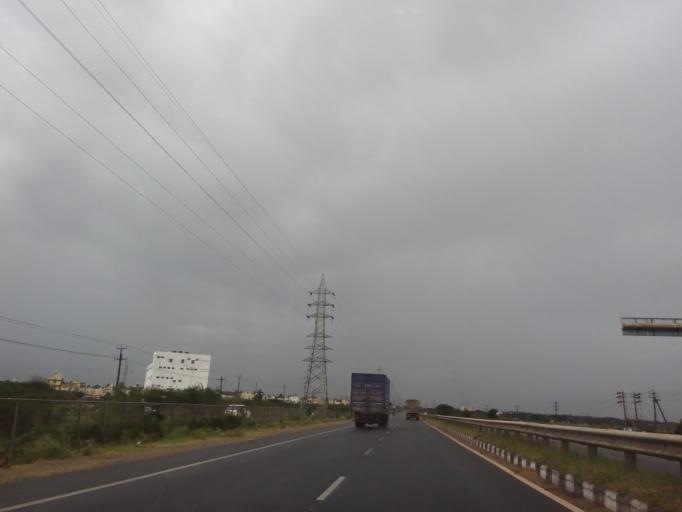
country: IN
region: Karnataka
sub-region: Davanagere
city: Harihar
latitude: 14.4386
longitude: 75.9054
